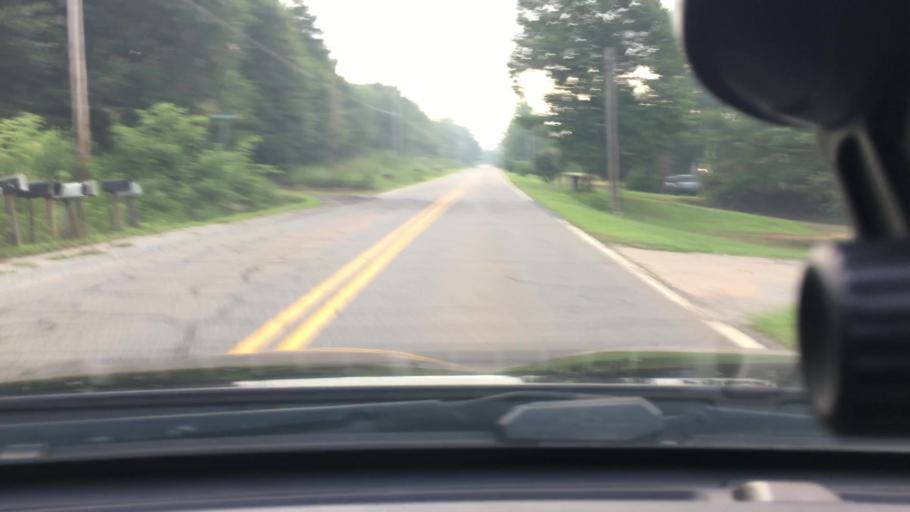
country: US
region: North Carolina
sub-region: Rutherford County
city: Rutherfordton
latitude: 35.3764
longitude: -81.9742
